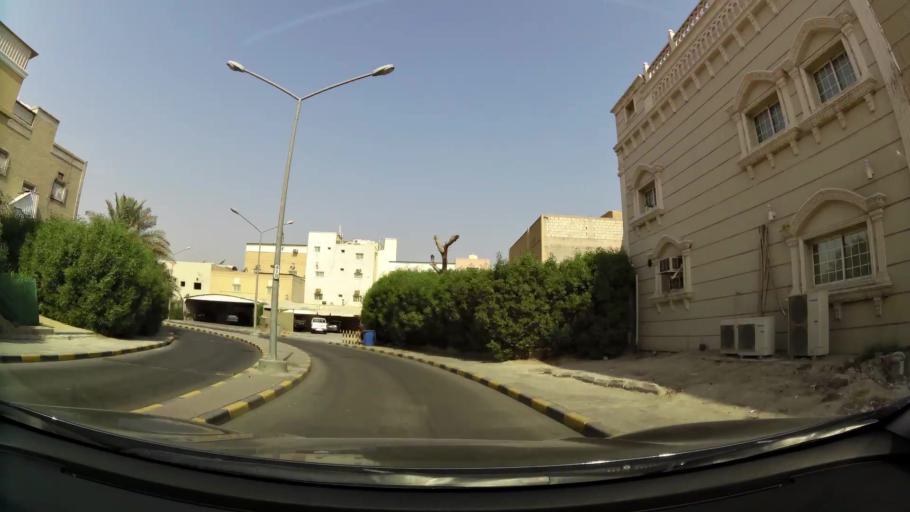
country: KW
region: Al Asimah
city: Ar Rabiyah
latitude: 29.2876
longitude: 47.8928
